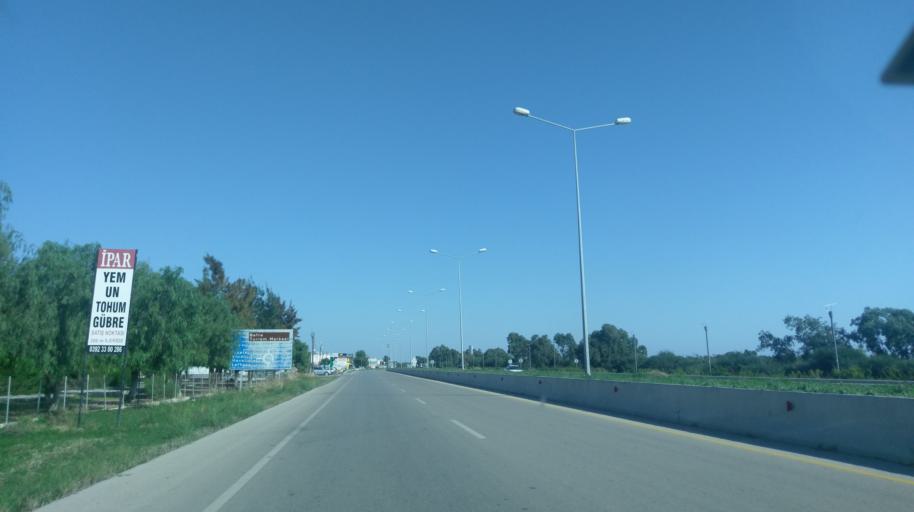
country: CY
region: Ammochostos
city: Trikomo
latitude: 35.2765
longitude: 33.9185
